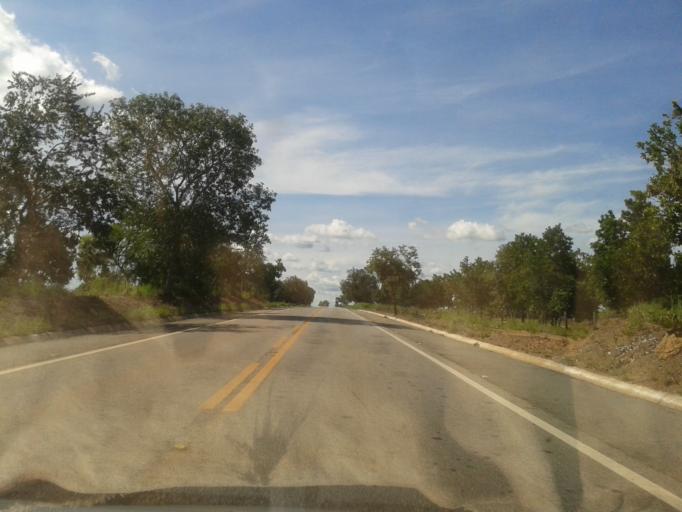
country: BR
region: Goias
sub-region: Mozarlandia
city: Mozarlandia
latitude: -15.2606
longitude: -50.4919
